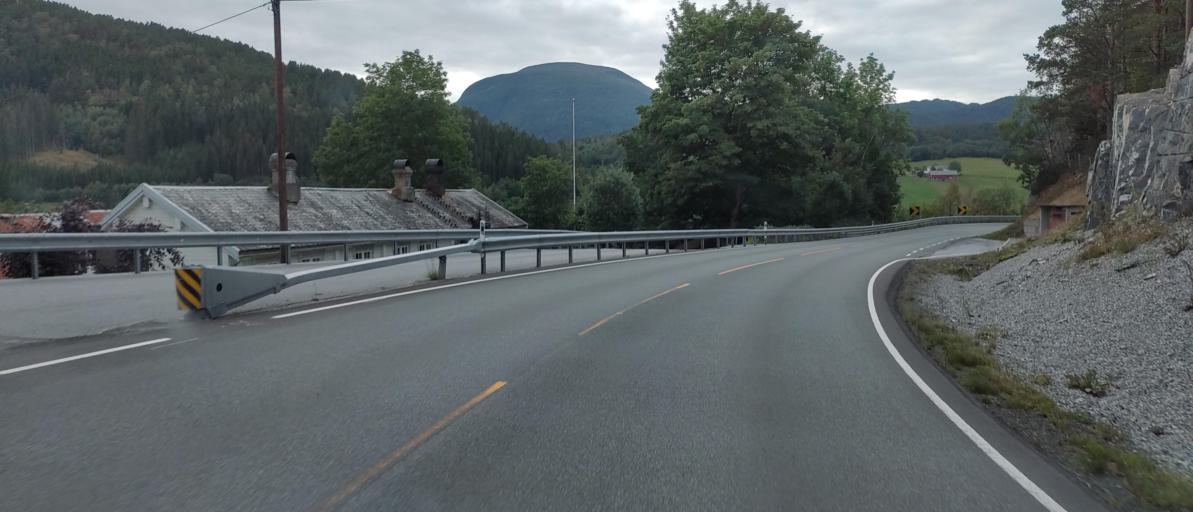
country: NO
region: More og Romsdal
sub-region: Rauma
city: Andalsnes
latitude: 62.5765
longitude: 7.5387
